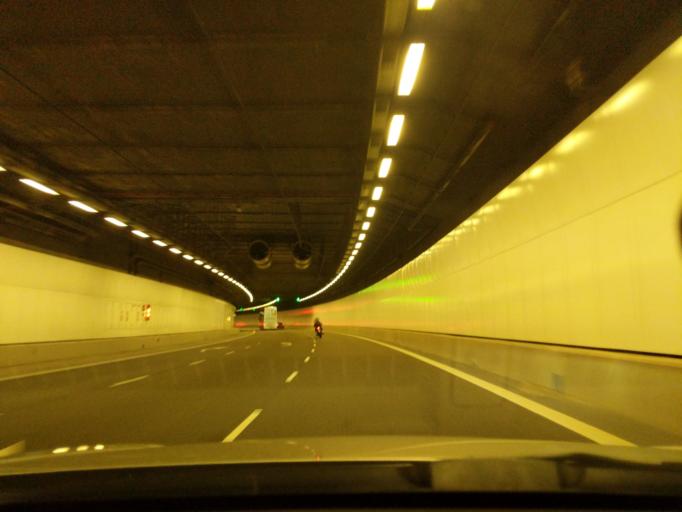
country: SG
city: Singapore
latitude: 1.2926
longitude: 103.8755
